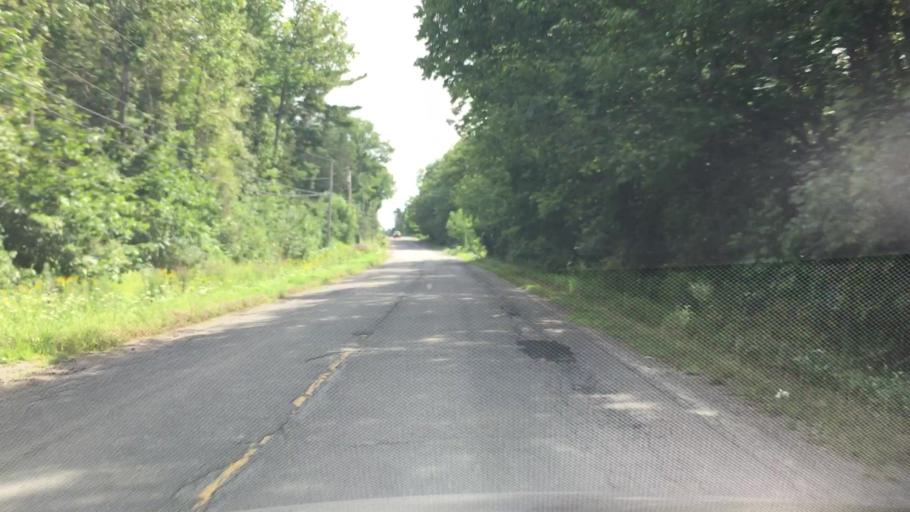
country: US
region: Maine
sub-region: Penobscot County
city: Hampden
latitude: 44.7262
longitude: -68.8640
